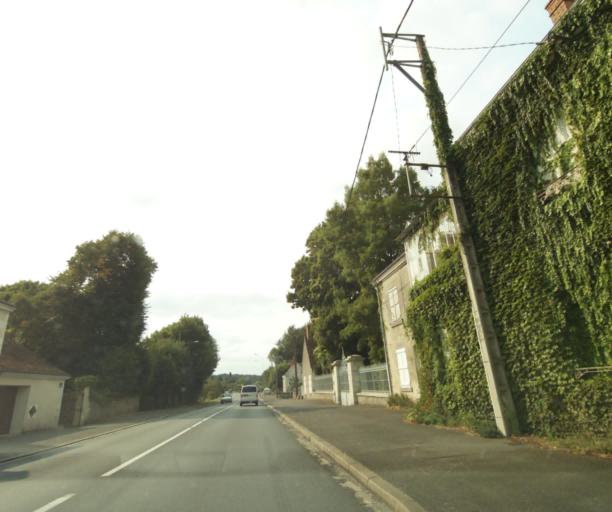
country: FR
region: Centre
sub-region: Departement de l'Indre
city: Clion
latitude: 46.9418
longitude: 1.2273
